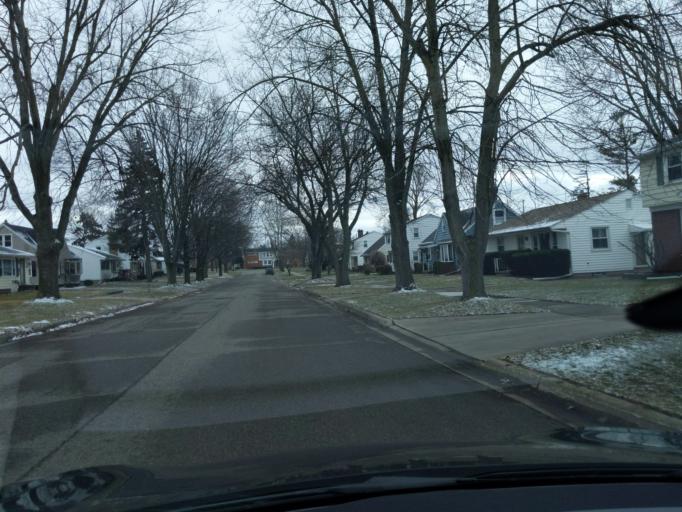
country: US
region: Michigan
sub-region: Ingham County
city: East Lansing
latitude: 42.7463
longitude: -84.5189
